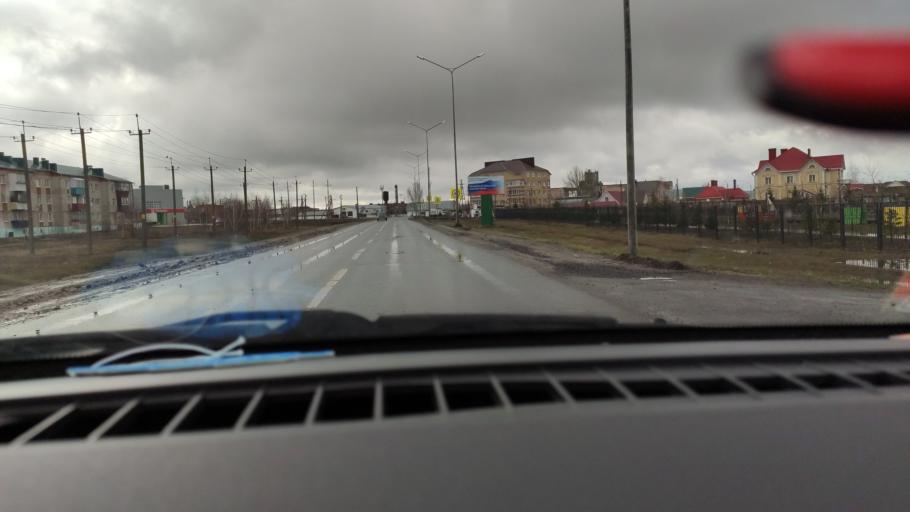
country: RU
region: Tatarstan
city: Nurlat
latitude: 54.4321
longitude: 50.8154
